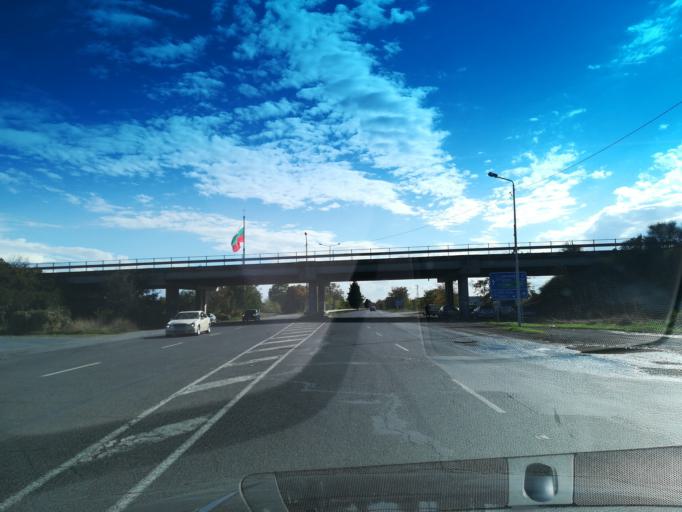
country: BG
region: Stara Zagora
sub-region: Obshtina Stara Zagora
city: Stara Zagora
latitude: 42.3945
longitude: 25.6455
